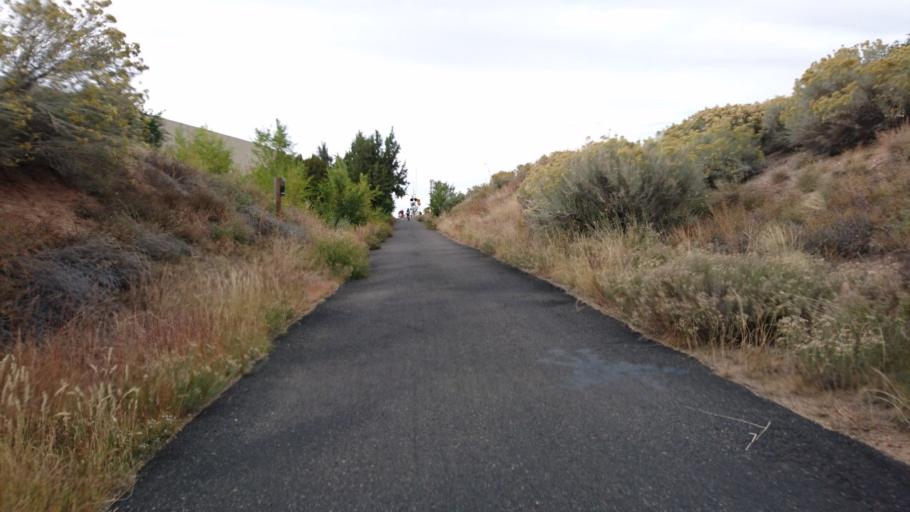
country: US
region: New Mexico
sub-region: Santa Fe County
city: Santa Fe
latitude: 35.6583
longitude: -105.9651
